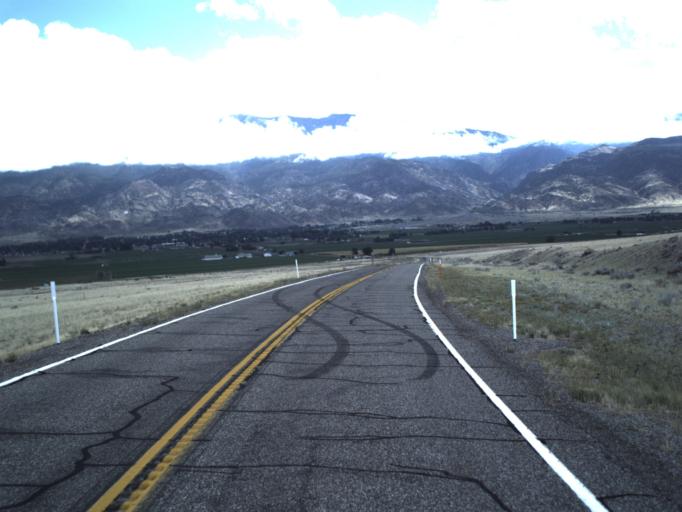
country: US
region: Utah
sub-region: Sevier County
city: Monroe
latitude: 38.6324
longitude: -112.1752
